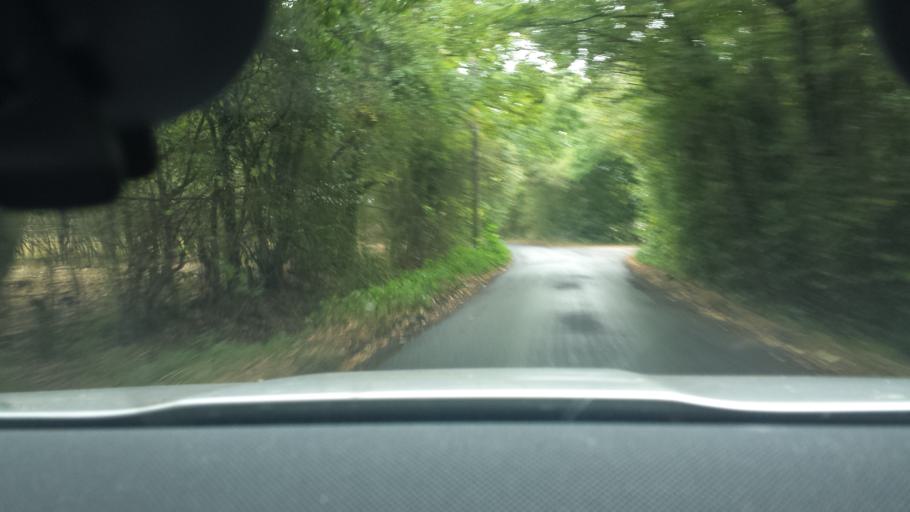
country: GB
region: England
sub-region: Kent
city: Staplehurst
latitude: 51.1768
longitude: 0.5434
